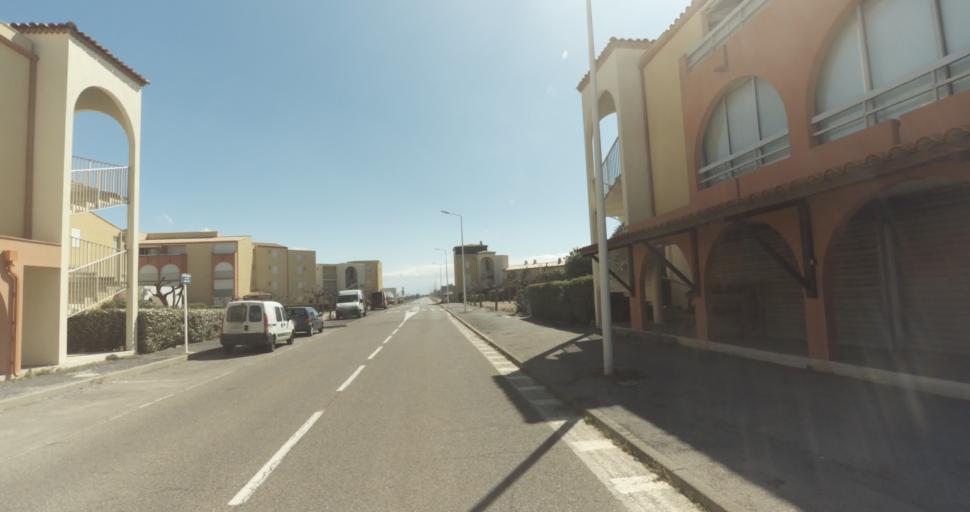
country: FR
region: Languedoc-Roussillon
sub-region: Departement des Pyrenees-Orientales
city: Le Barcares
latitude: 42.8469
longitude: 3.0422
